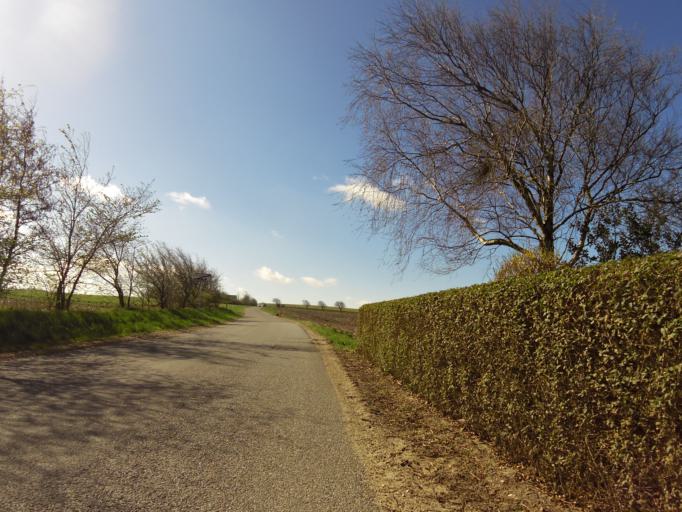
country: DK
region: Central Jutland
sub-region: Holstebro Kommune
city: Vinderup
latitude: 56.4670
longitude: 8.7214
